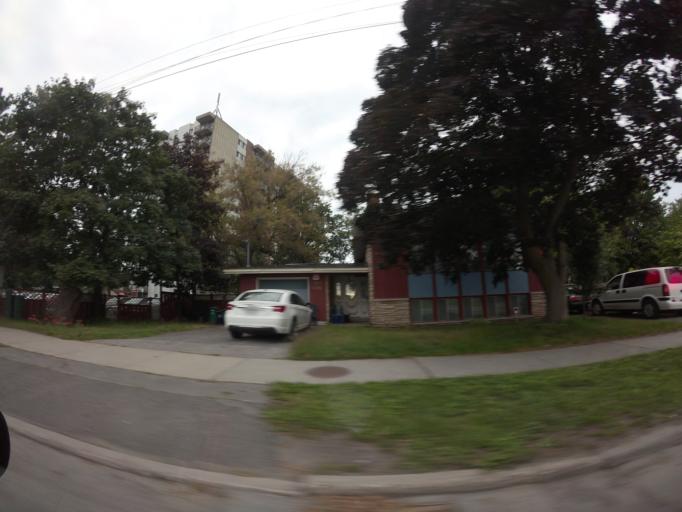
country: CA
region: Ontario
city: Ottawa
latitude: 45.4351
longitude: -75.6436
